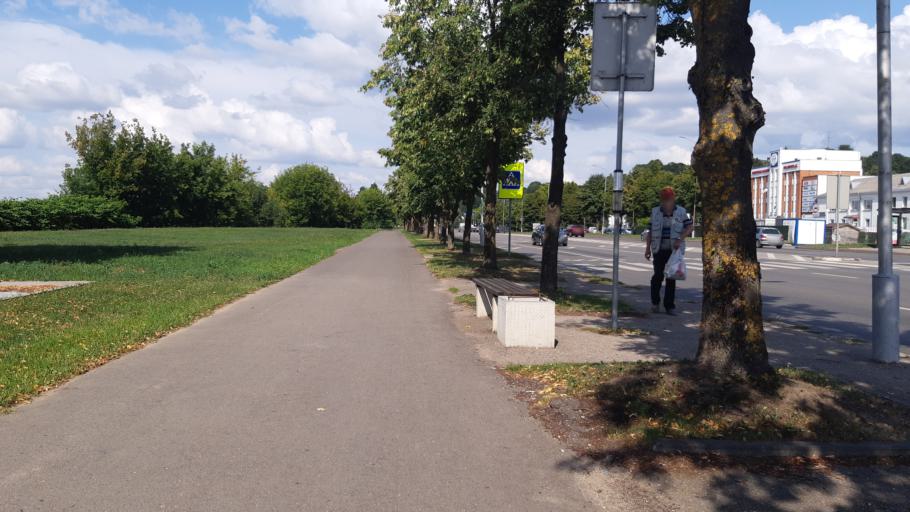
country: LT
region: Kauno apskritis
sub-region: Kaunas
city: Kaunas
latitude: 54.9053
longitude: 23.8992
